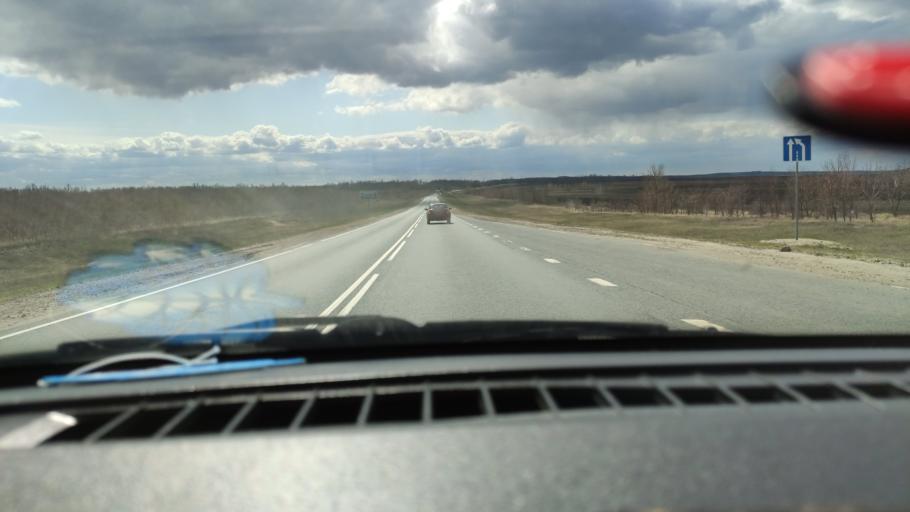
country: RU
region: Saratov
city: Alekseyevka
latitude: 52.2828
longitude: 47.9317
